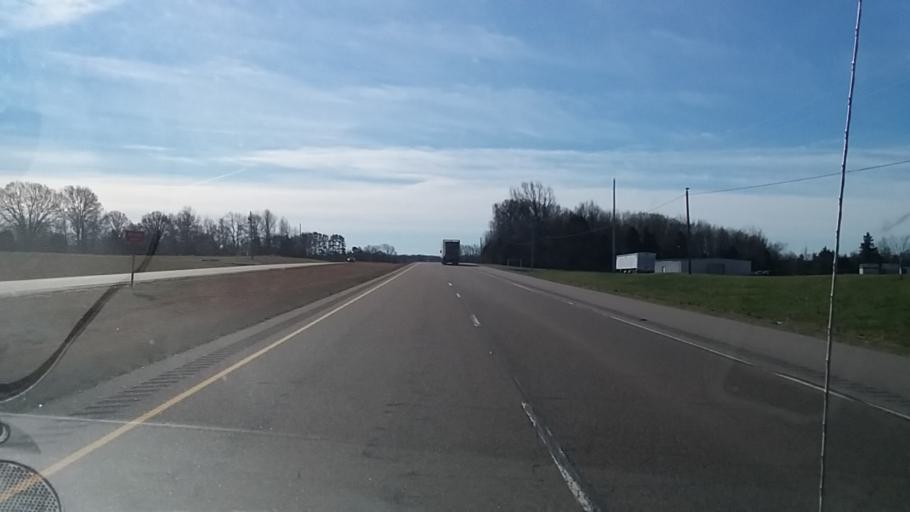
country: US
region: Tennessee
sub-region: Crockett County
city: Alamo
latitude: 35.8621
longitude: -89.2071
